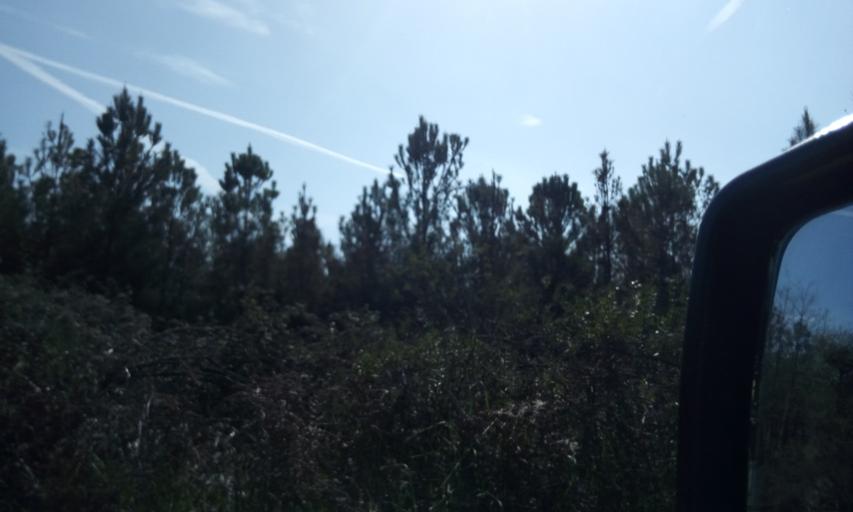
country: PT
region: Guarda
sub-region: Fornos de Algodres
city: Fornos de Algodres
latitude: 40.6217
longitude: -7.4743
